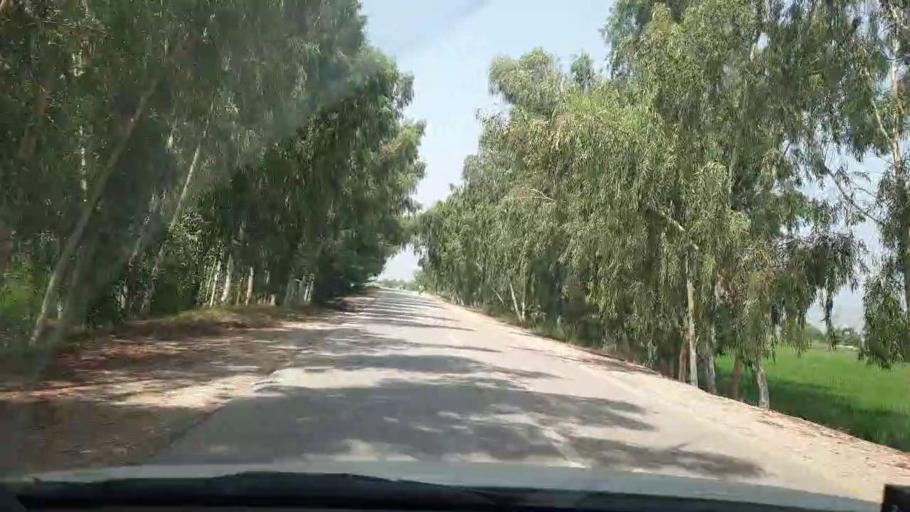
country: PK
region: Sindh
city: Rustam jo Goth
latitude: 27.9572
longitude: 68.7421
